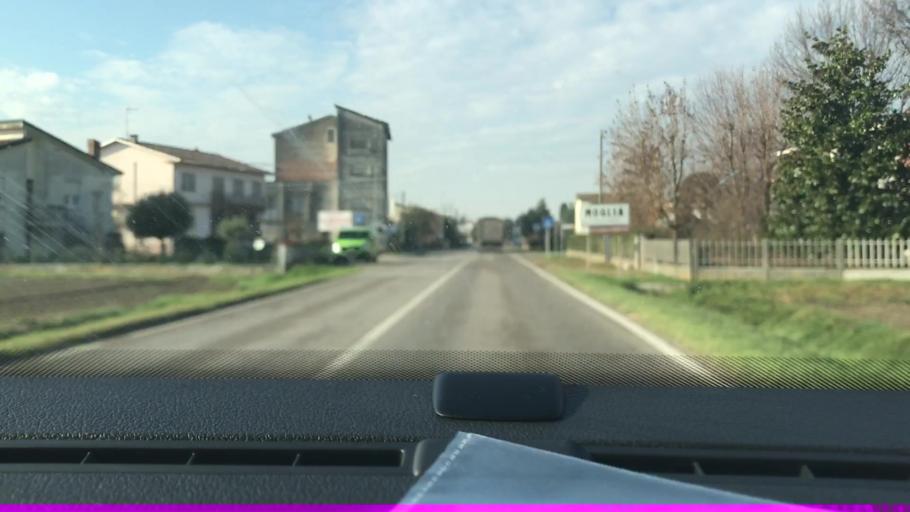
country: IT
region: Lombardy
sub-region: Provincia di Mantova
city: Sermide
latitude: 45.0104
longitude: 11.2750
